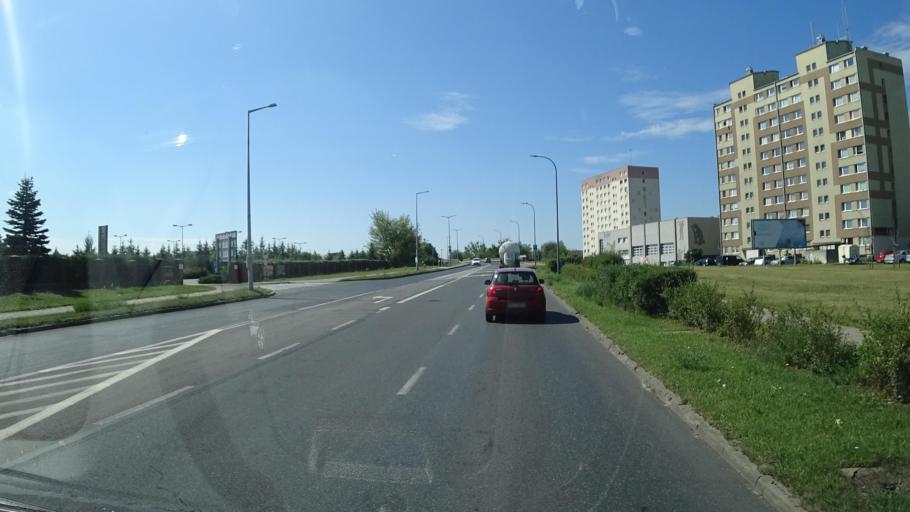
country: PL
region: Greater Poland Voivodeship
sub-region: Konin
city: Konin
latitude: 52.2333
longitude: 18.2680
